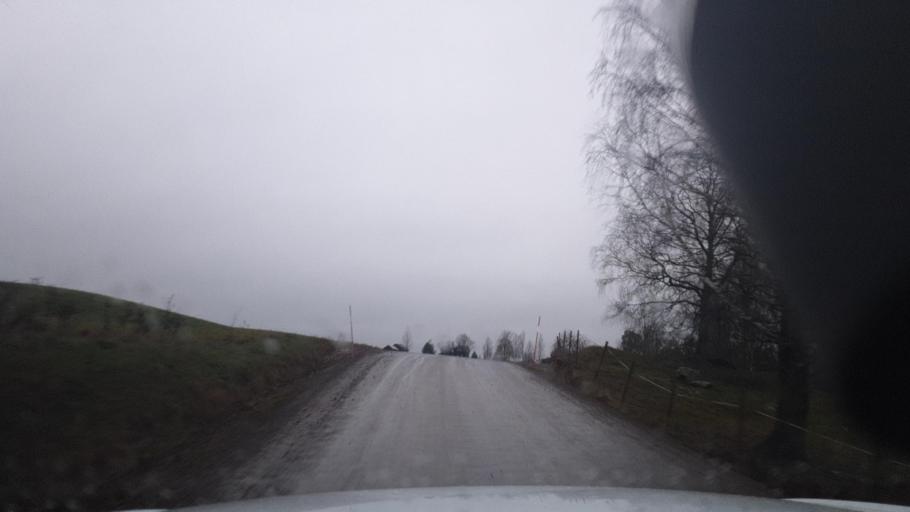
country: SE
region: Vaermland
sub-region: Eda Kommun
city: Amotfors
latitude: 59.7214
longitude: 12.1434
